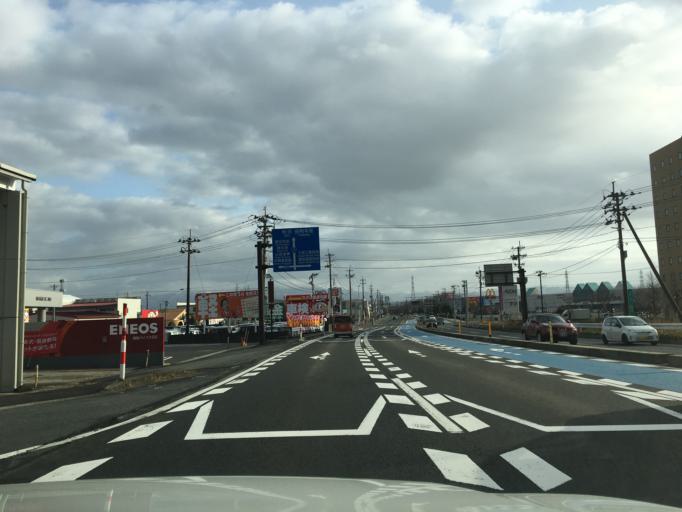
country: JP
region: Yamagata
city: Sakata
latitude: 38.8909
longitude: 139.8487
